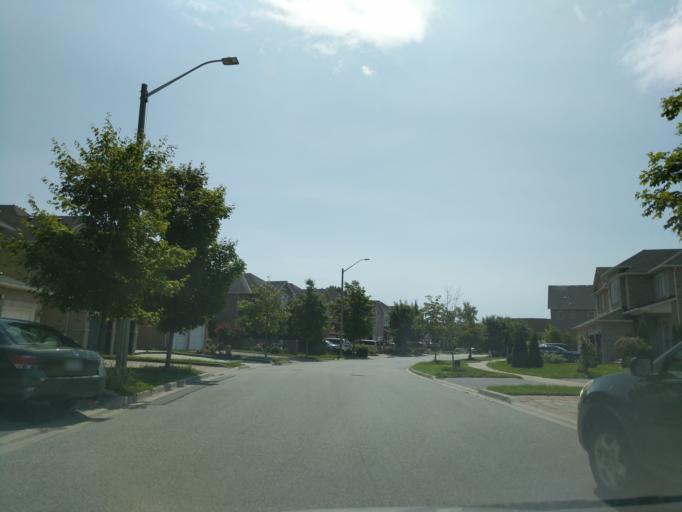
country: CA
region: Ontario
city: Markham
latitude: 43.8462
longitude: -79.2447
